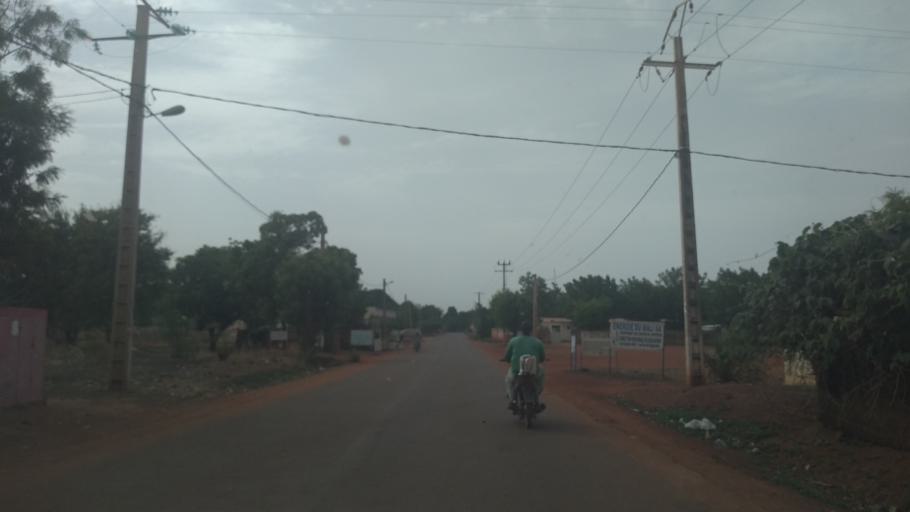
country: ML
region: Bamako
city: Bamako
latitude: 12.6179
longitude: -7.7788
